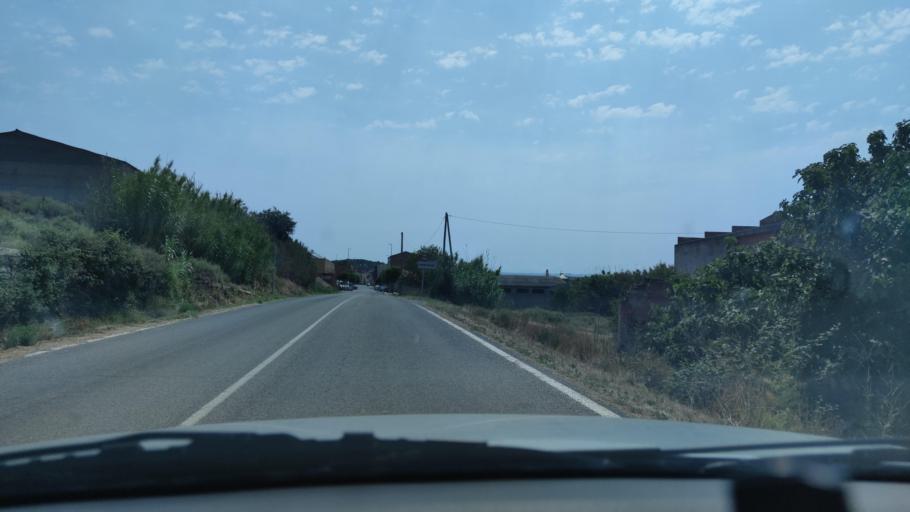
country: ES
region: Catalonia
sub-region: Provincia de Lleida
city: Bellpuig
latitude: 41.6085
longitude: 1.0326
